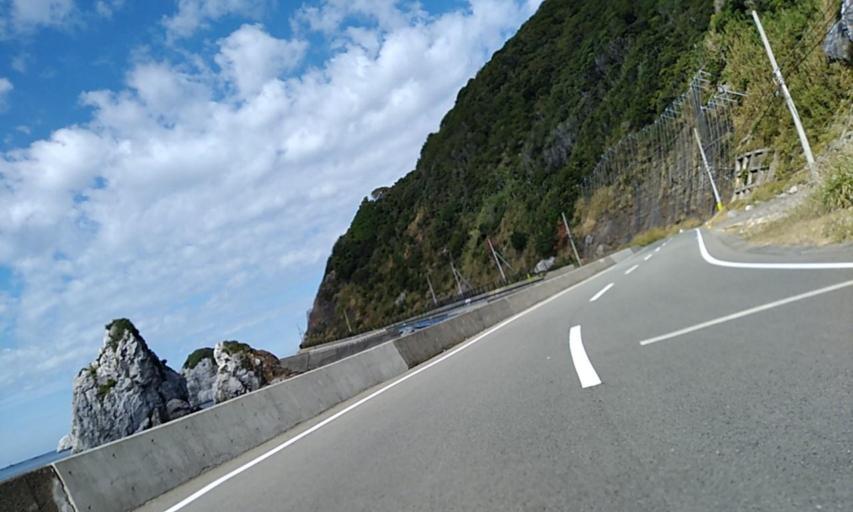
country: JP
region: Wakayama
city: Gobo
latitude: 33.9723
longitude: 135.0789
